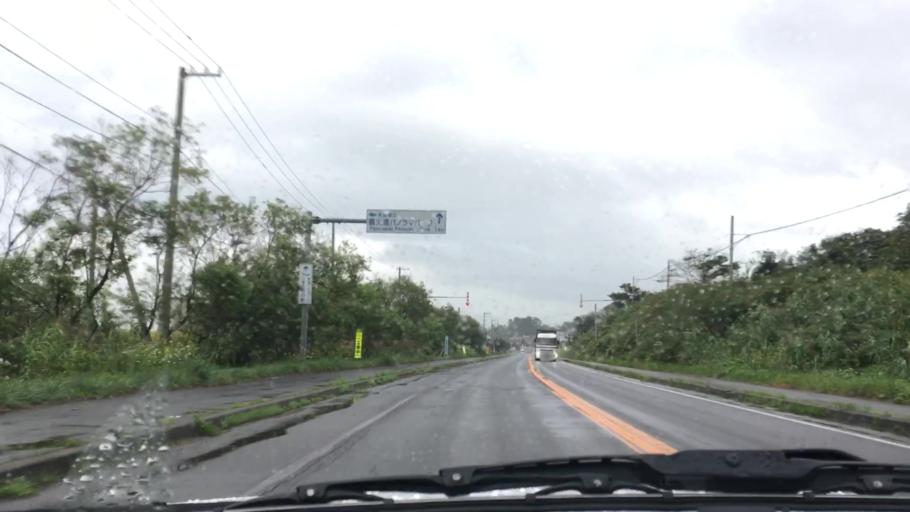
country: JP
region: Hokkaido
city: Nanae
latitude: 42.2389
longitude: 140.3028
